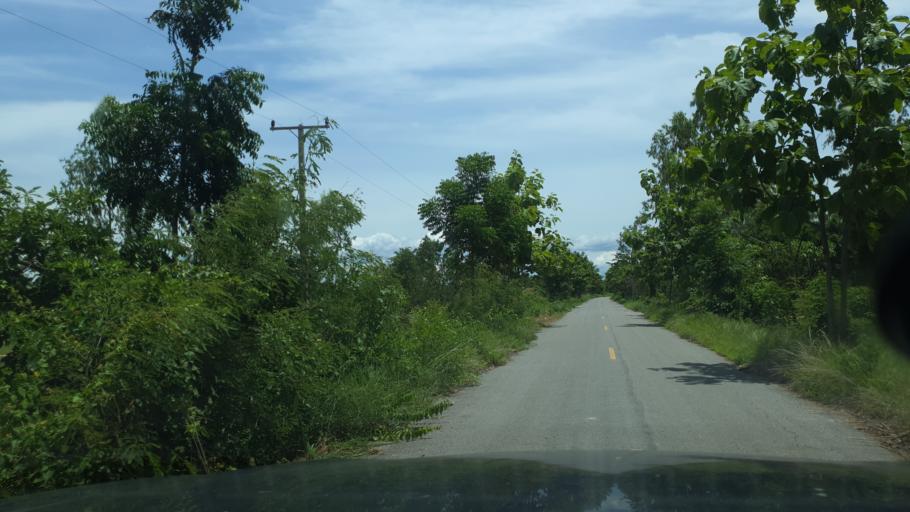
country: TH
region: Sukhothai
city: Ban Na
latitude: 17.1127
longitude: 99.6773
